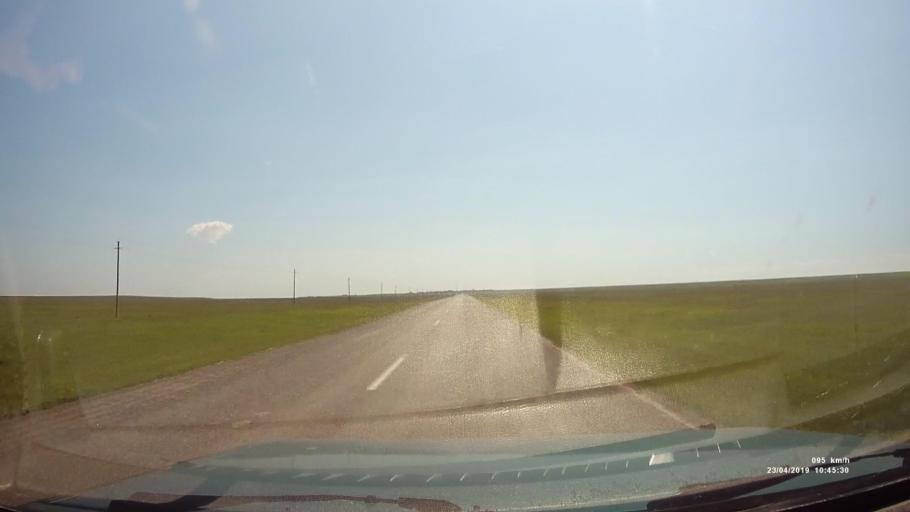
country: RU
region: Kalmykiya
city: Yashalta
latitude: 46.4508
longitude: 42.6757
